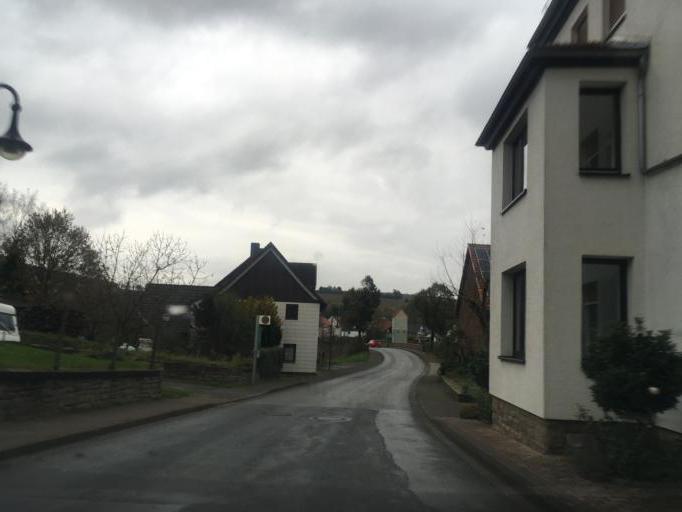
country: DE
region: Lower Saxony
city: Uslar
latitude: 51.6265
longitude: 9.6218
